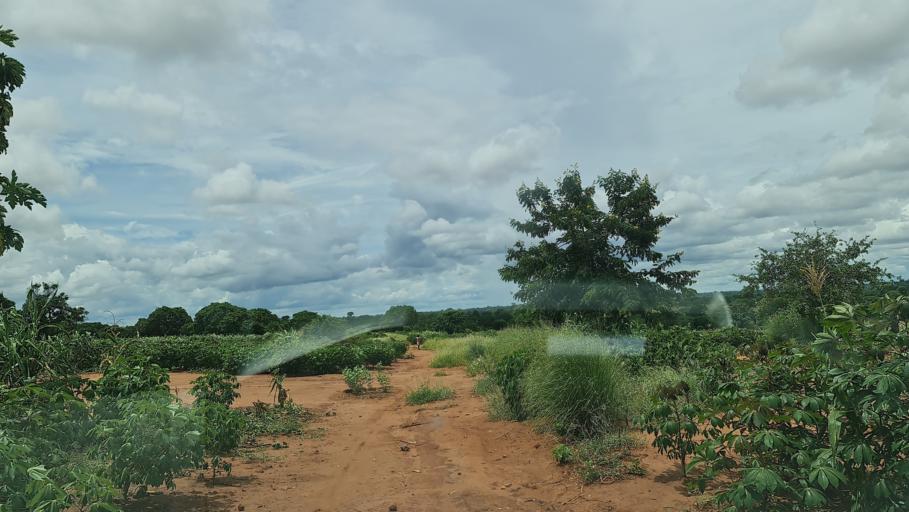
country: MZ
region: Nampula
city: Nacala
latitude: -14.7848
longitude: 39.9805
